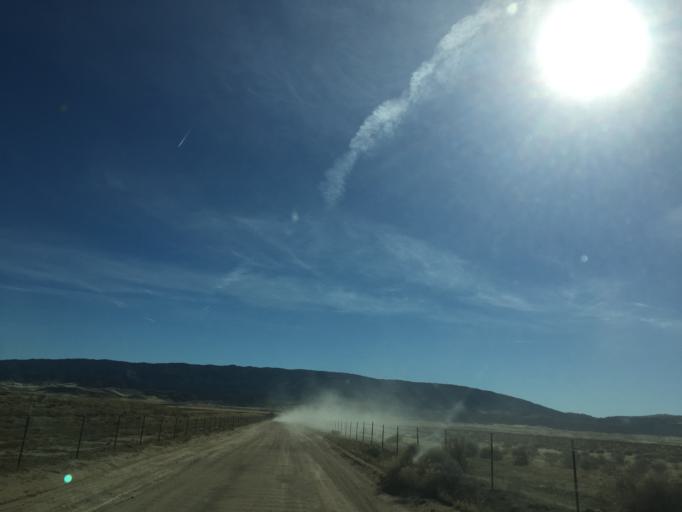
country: US
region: California
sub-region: Kern County
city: Lebec
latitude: 34.8239
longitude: -118.6609
